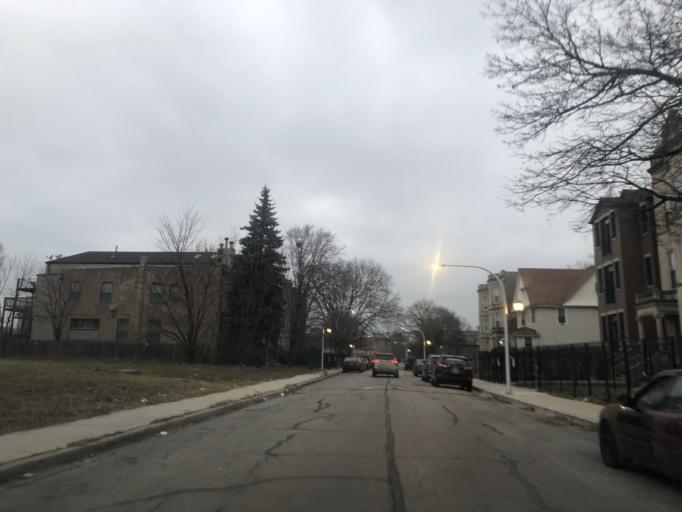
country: US
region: Illinois
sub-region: Cook County
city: Chicago
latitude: 41.7788
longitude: -87.6029
